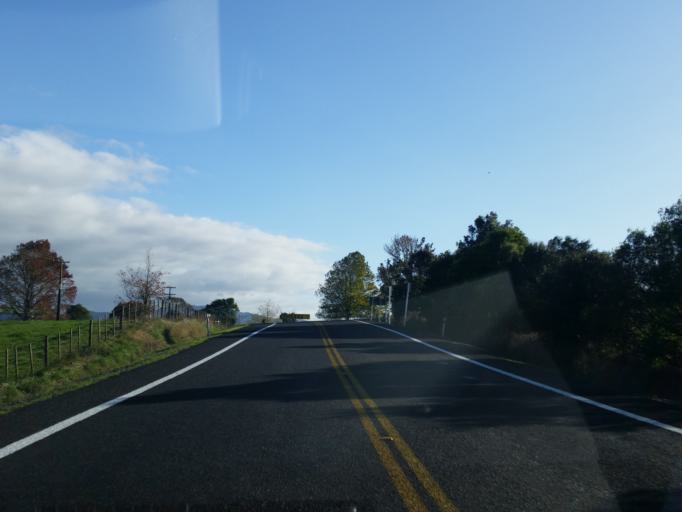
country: NZ
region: Bay of Plenty
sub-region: Western Bay of Plenty District
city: Waihi Beach
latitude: -37.4424
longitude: 175.8759
